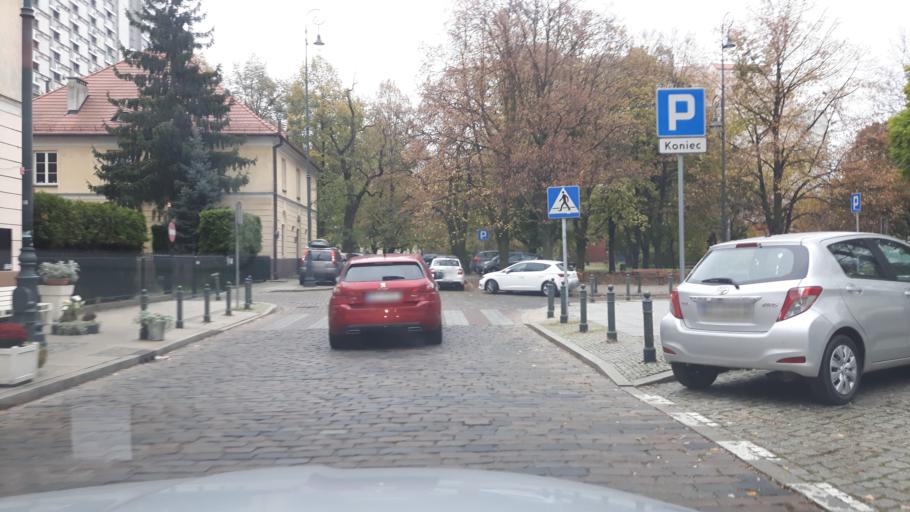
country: PL
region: Masovian Voivodeship
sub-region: Warszawa
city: Wola
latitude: 52.2384
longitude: 20.9935
